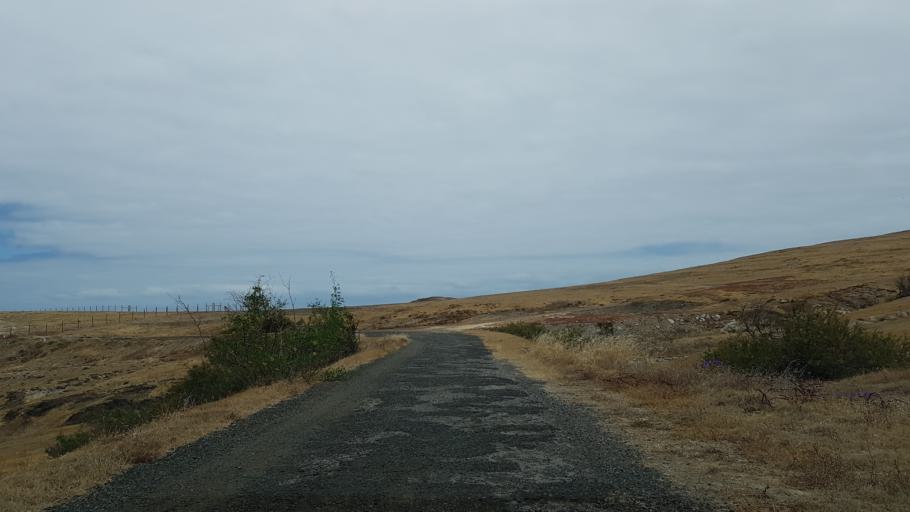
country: PT
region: Madeira
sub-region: Porto Santo
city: Camacha
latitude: 33.0916
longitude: -16.3357
